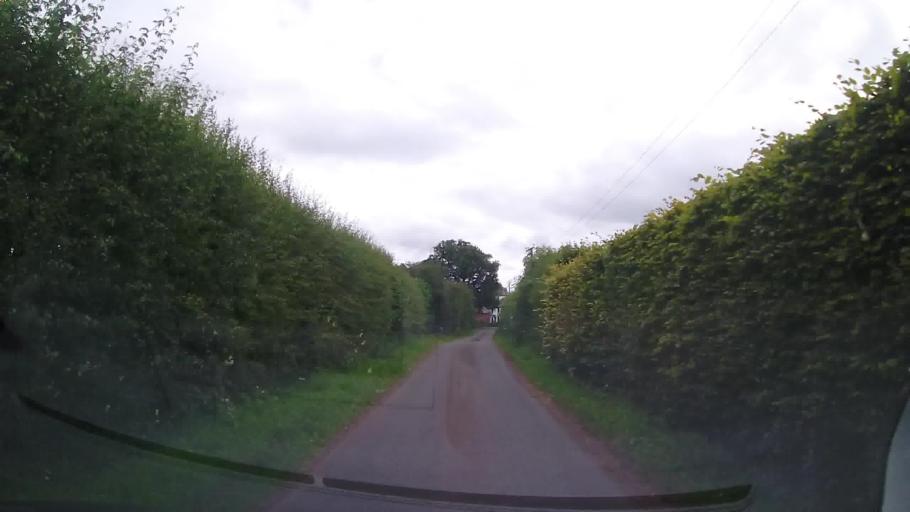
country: GB
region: England
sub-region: Shropshire
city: Prees
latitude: 52.9067
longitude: -2.7058
